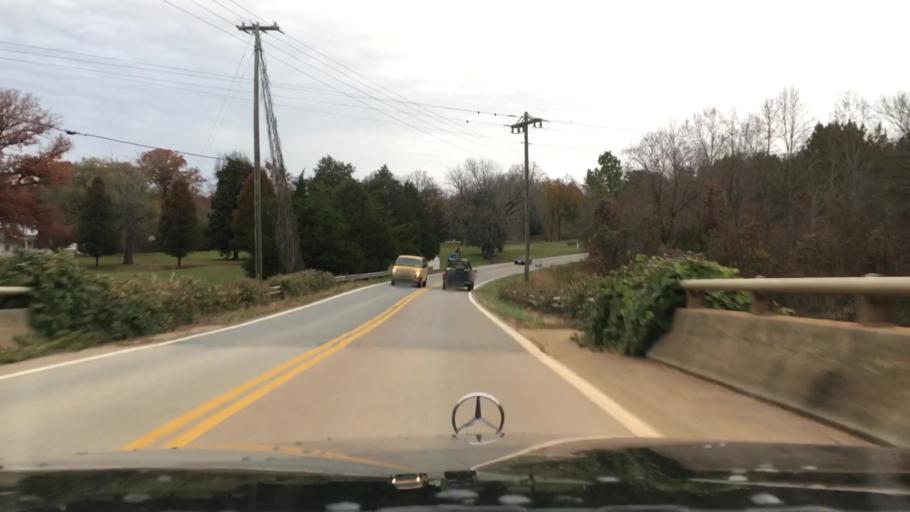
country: US
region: Virginia
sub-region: Campbell County
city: Timberlake
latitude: 37.2262
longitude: -79.2856
